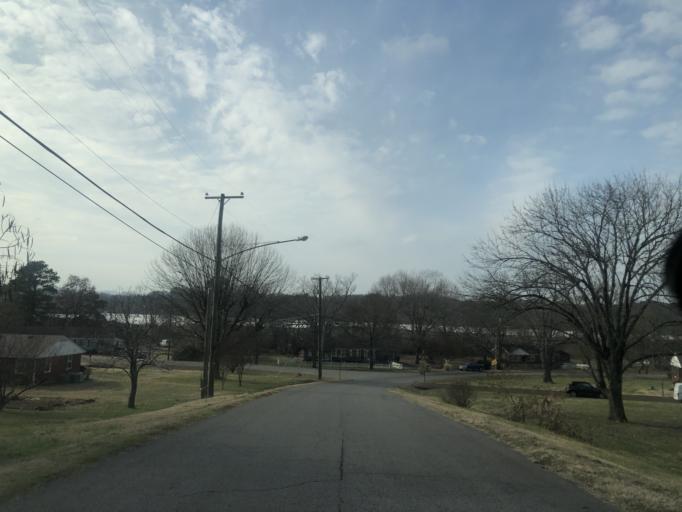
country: US
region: Tennessee
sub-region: Davidson County
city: Oak Hill
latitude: 36.1041
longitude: -86.7062
